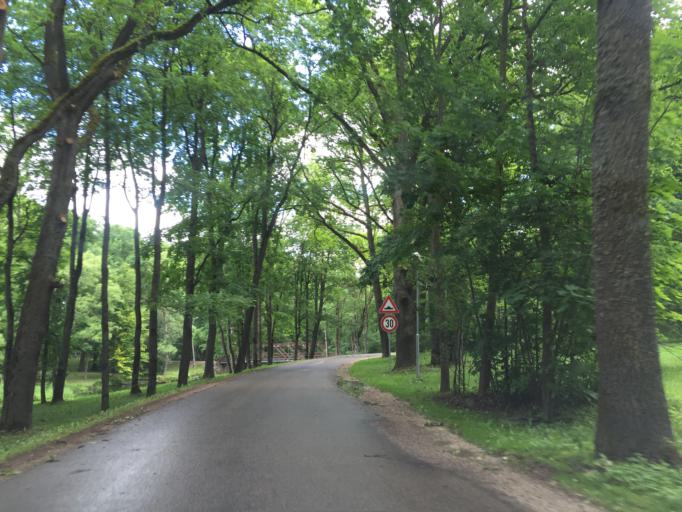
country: LV
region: Lecava
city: Iecava
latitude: 56.5932
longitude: 24.1978
